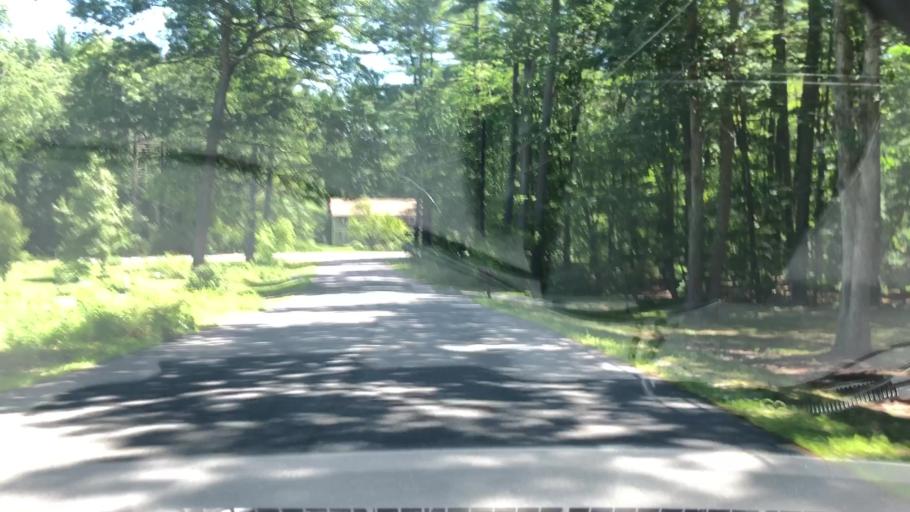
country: US
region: New Hampshire
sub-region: Hillsborough County
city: Milford
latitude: 42.8353
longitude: -71.5777
